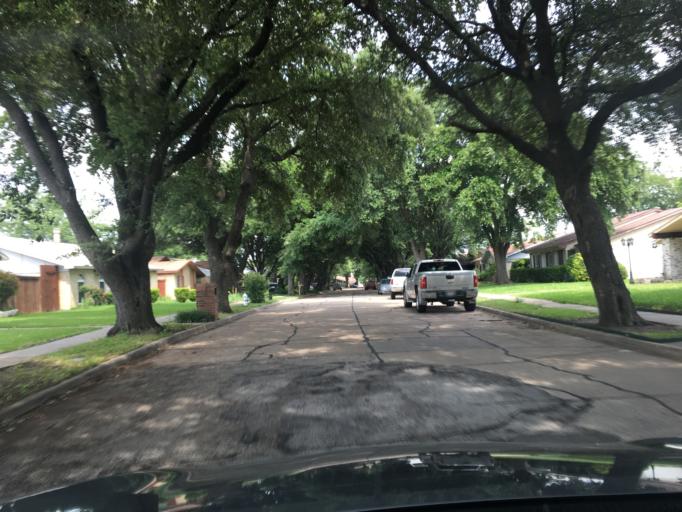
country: US
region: Texas
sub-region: Dallas County
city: Richardson
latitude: 32.9579
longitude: -96.6813
